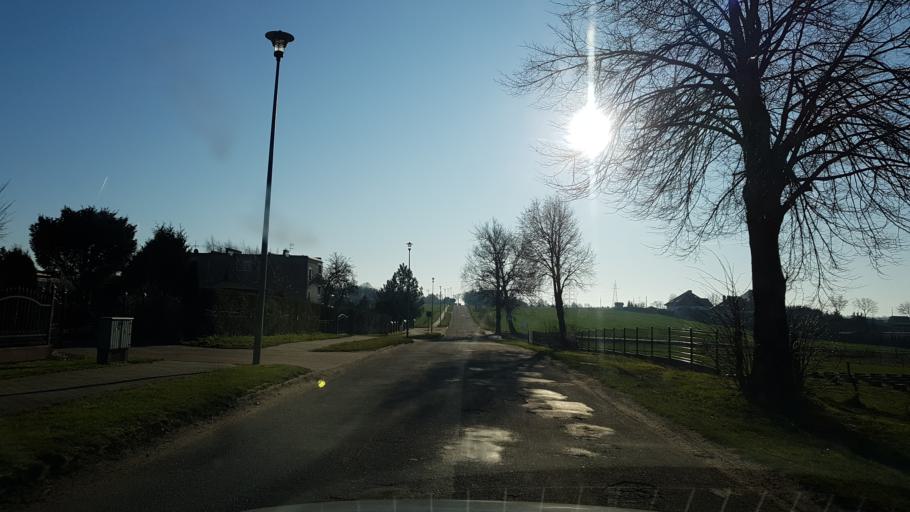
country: PL
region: West Pomeranian Voivodeship
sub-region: Powiat kolobrzeski
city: Ustronie Morskie
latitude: 54.2036
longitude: 15.7375
